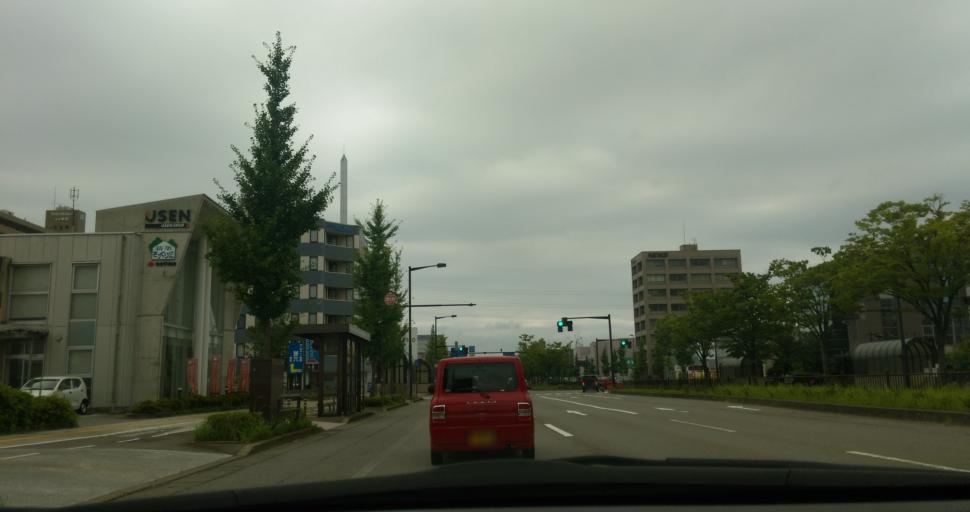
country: JP
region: Ishikawa
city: Kanazawa-shi
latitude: 36.5886
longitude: 136.6339
